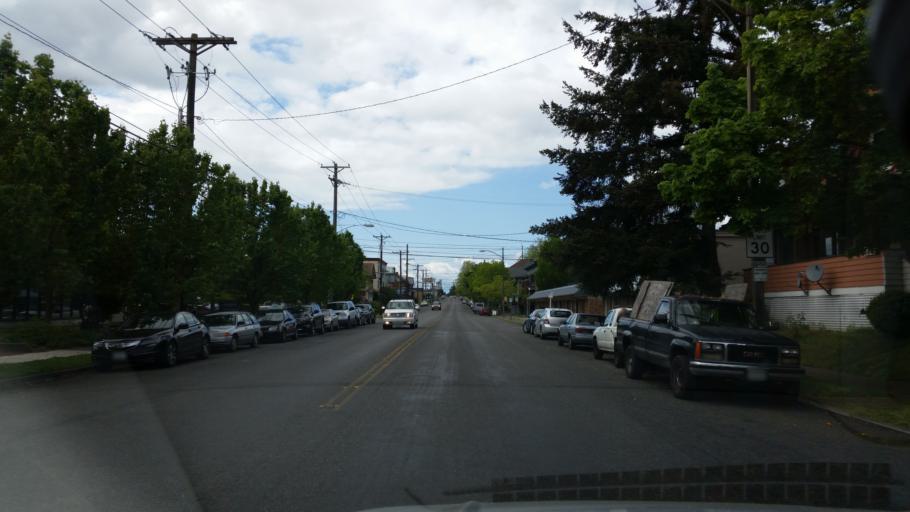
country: US
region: Washington
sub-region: Pierce County
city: Tacoma
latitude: 47.2571
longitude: -122.4541
